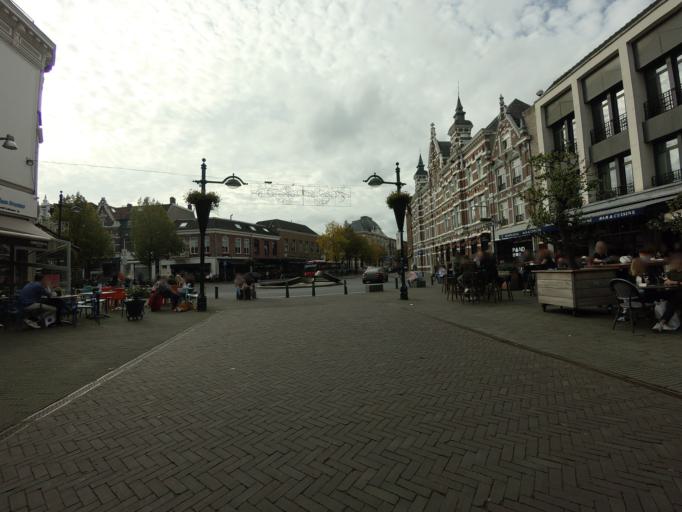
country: NL
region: North Brabant
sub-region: Gemeente Breda
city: Breda
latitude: 51.5832
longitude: 4.7774
